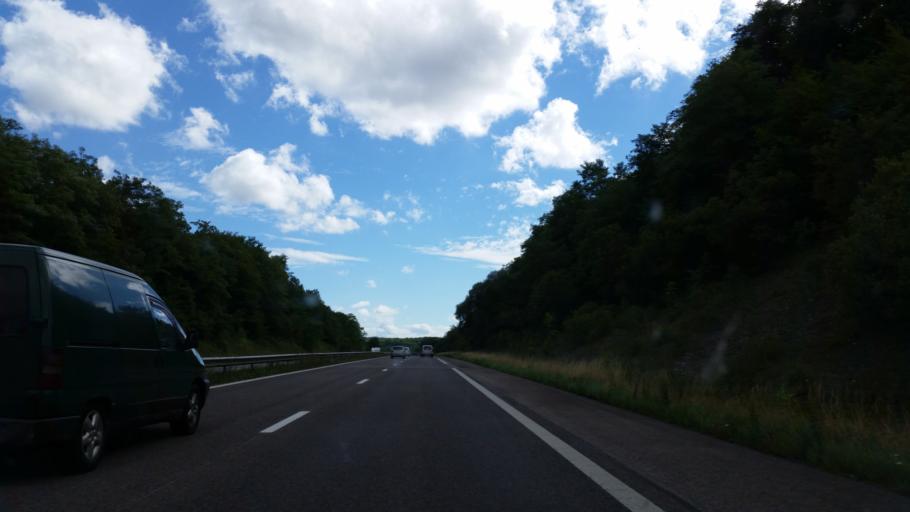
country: FR
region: Lorraine
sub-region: Departement de Meurthe-et-Moselle
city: Bayon
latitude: 48.4496
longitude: 6.2335
